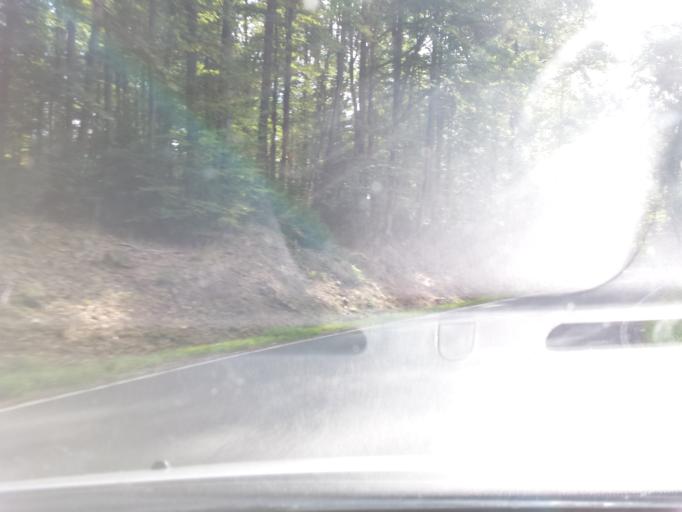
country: DE
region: Hesse
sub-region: Regierungsbezirk Kassel
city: Bad Hersfeld
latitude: 50.8702
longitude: 9.6564
